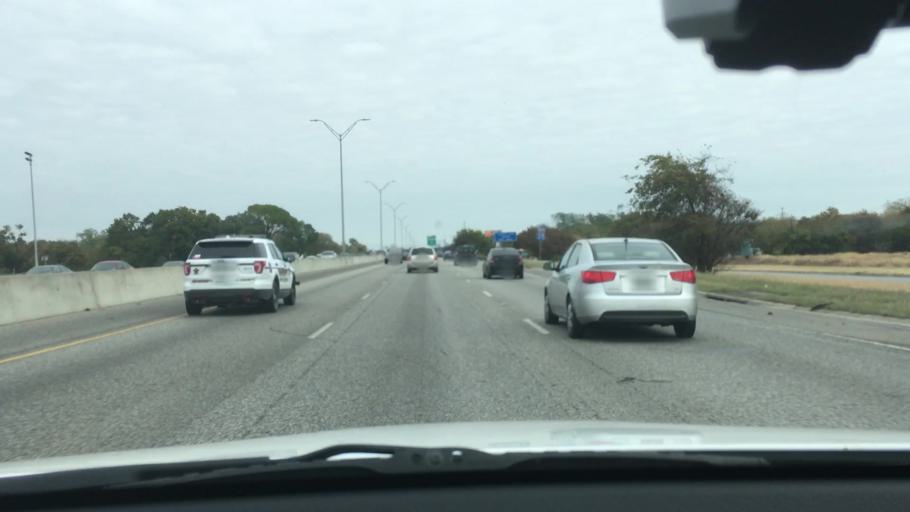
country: US
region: Texas
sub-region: Hays County
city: San Marcos
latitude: 29.8731
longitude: -97.9336
